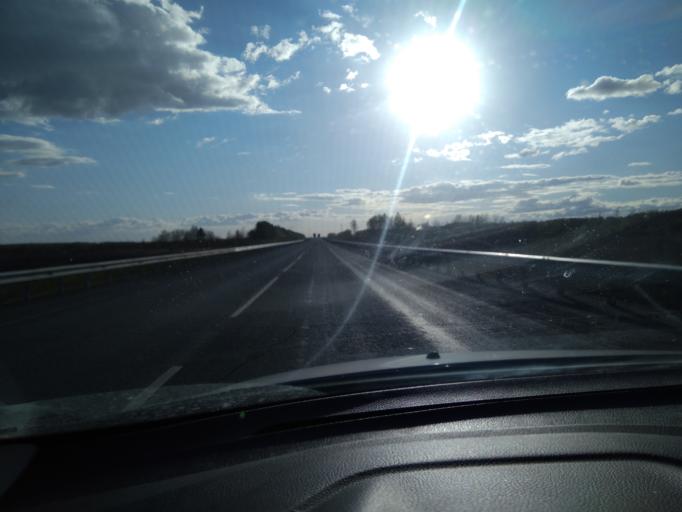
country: RU
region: Sverdlovsk
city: Troitskiy
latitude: 57.0862
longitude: 63.7125
